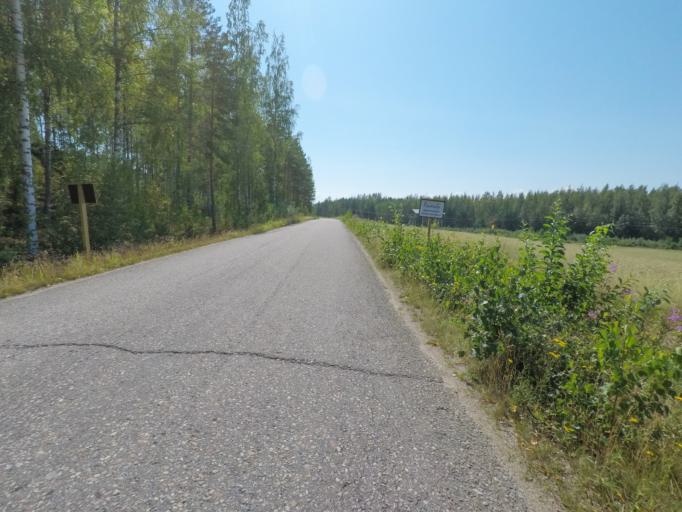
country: FI
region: Southern Savonia
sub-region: Mikkeli
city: Puumala
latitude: 61.4156
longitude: 28.0921
